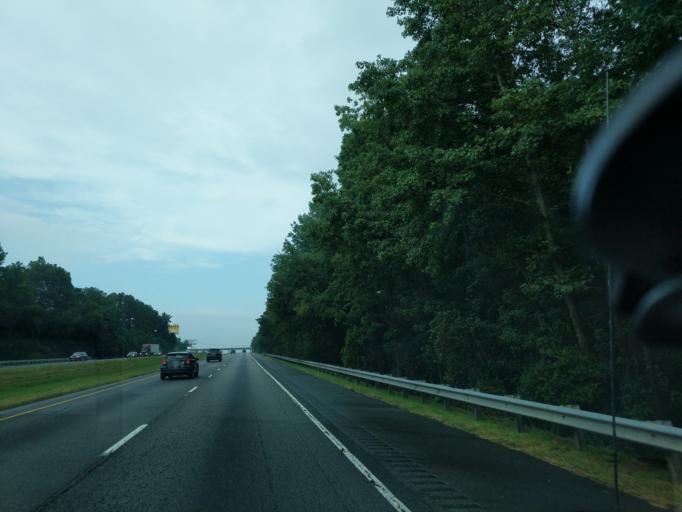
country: US
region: Georgia
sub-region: Franklin County
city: Carnesville
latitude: 34.4030
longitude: -83.2036
